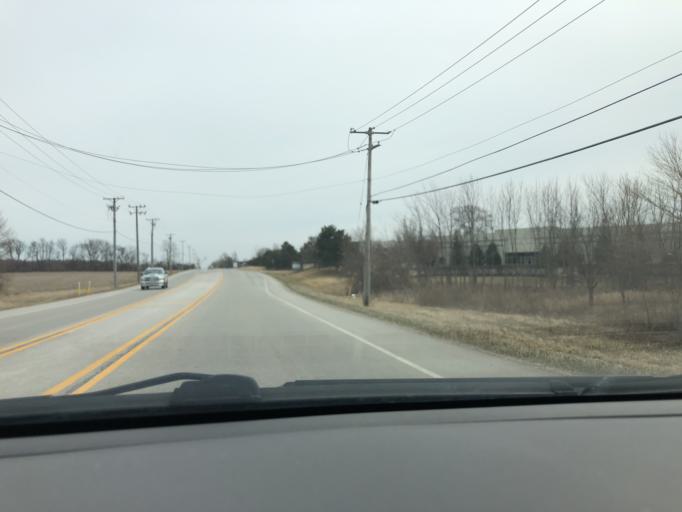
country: US
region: Illinois
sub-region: Kane County
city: Gilberts
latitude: 42.0692
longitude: -88.3446
